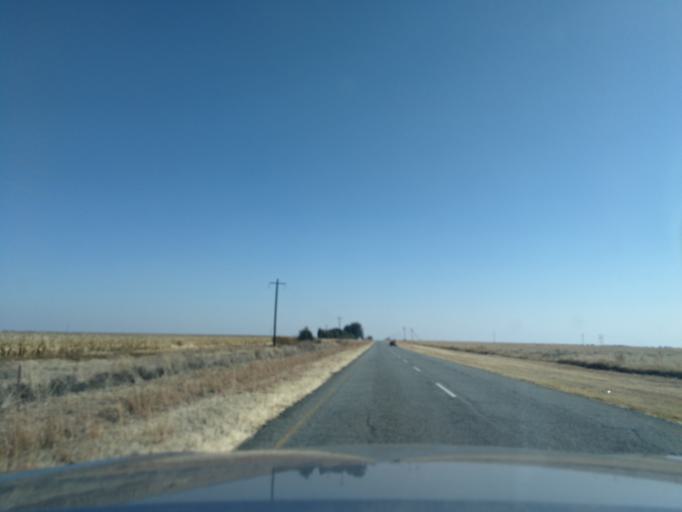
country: ZA
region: Orange Free State
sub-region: Fezile Dabi District Municipality
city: Viljoenskroon
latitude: -27.3808
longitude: 27.0464
